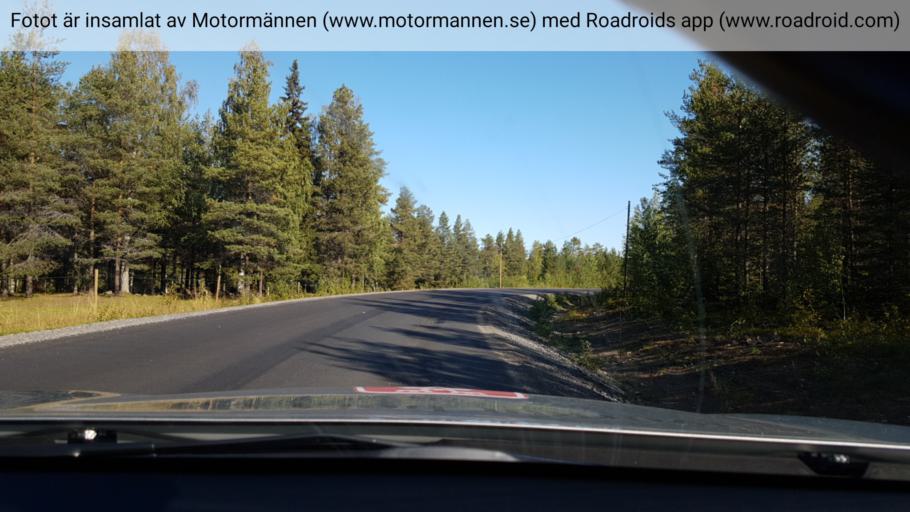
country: SE
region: Vaesterbotten
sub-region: Norsjo Kommun
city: Norsjoe
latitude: 64.8948
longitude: 19.4526
